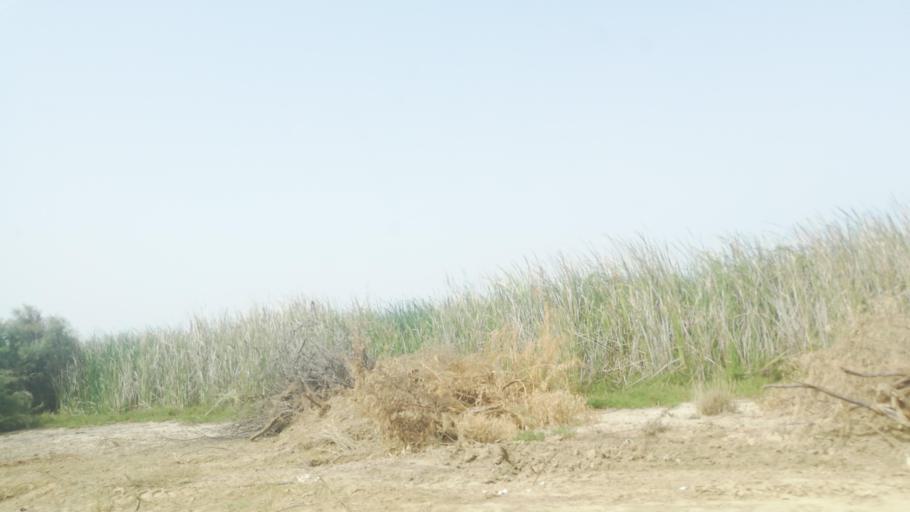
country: SN
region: Saint-Louis
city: Saint-Louis
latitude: 16.0623
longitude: -16.3136
